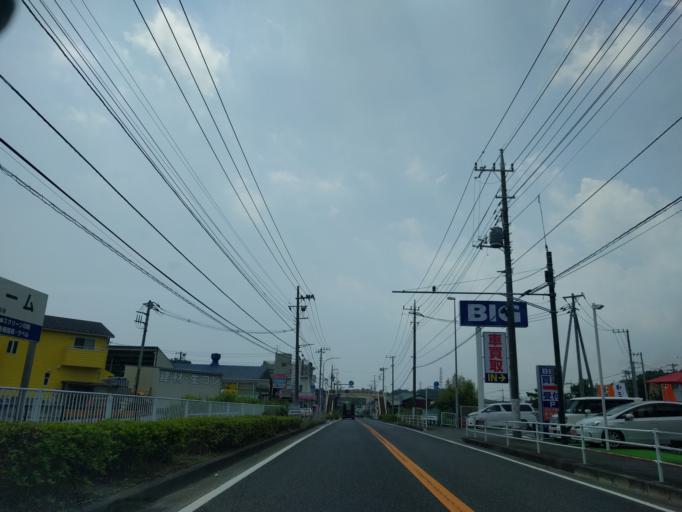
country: JP
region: Kanagawa
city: Minami-rinkan
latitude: 35.4950
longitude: 139.5055
